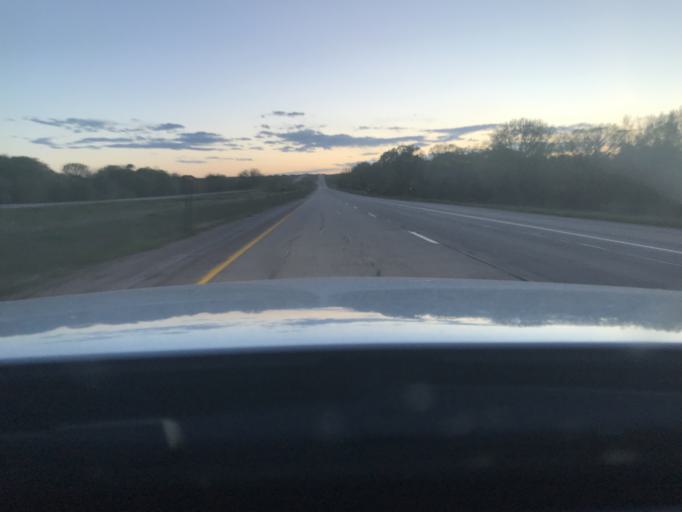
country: US
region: Wyoming
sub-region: Converse County
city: Glenrock
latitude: 42.8374
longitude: -105.8678
